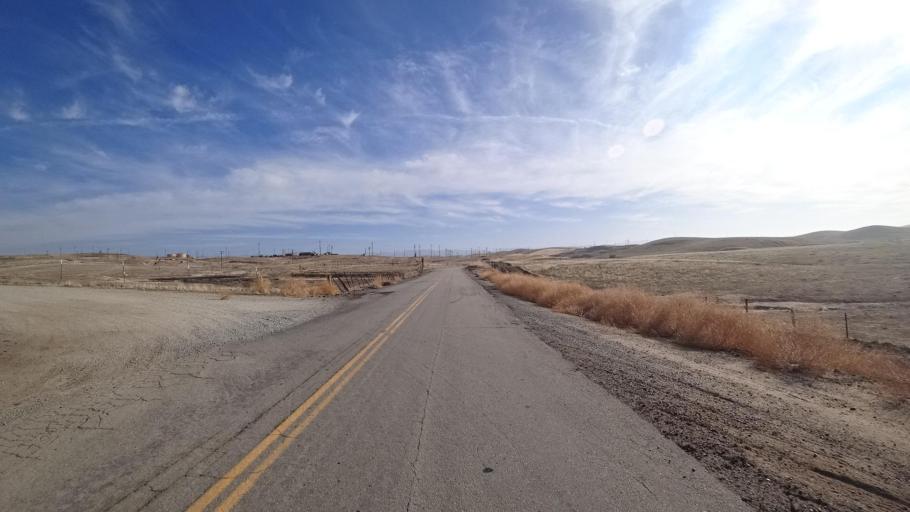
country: US
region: California
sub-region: Tulare County
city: Richgrove
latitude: 35.6265
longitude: -118.9915
